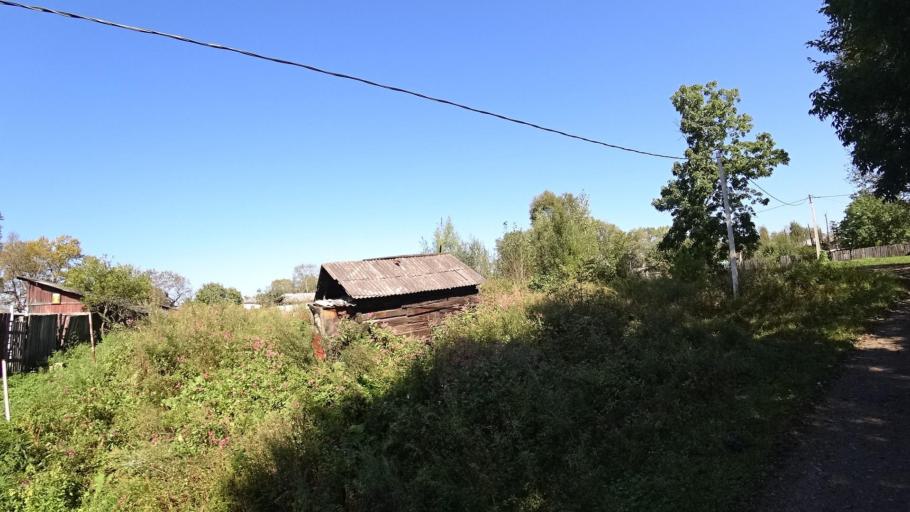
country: RU
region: Jewish Autonomous Oblast
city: Bira
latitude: 49.0019
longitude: 132.4691
